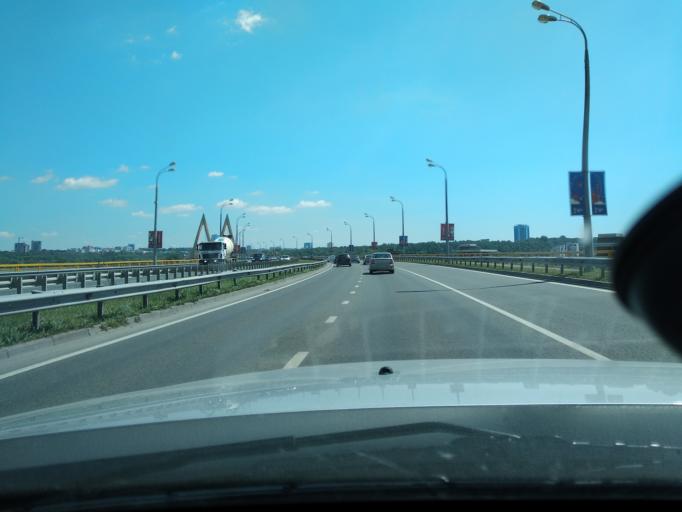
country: RU
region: Tatarstan
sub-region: Gorod Kazan'
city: Kazan
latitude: 55.8090
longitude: 49.1360
